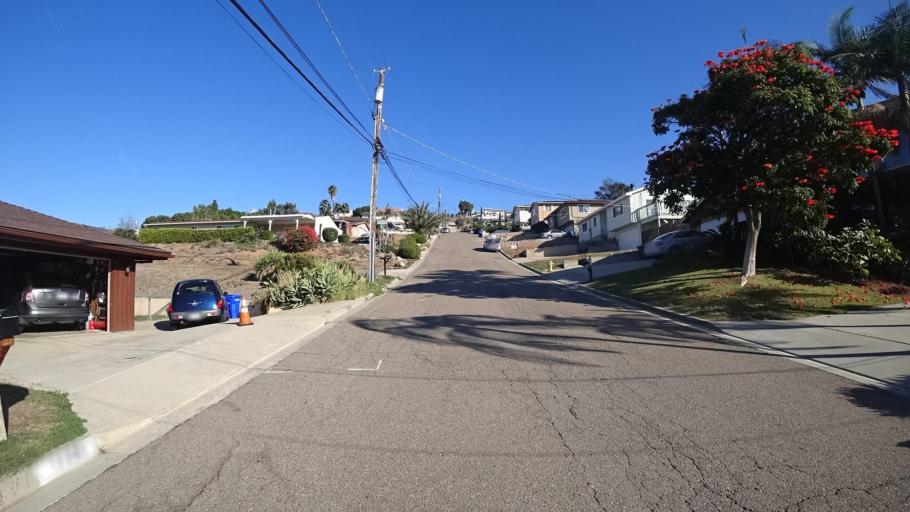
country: US
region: California
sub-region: San Diego County
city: La Presa
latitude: 32.7165
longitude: -116.9943
